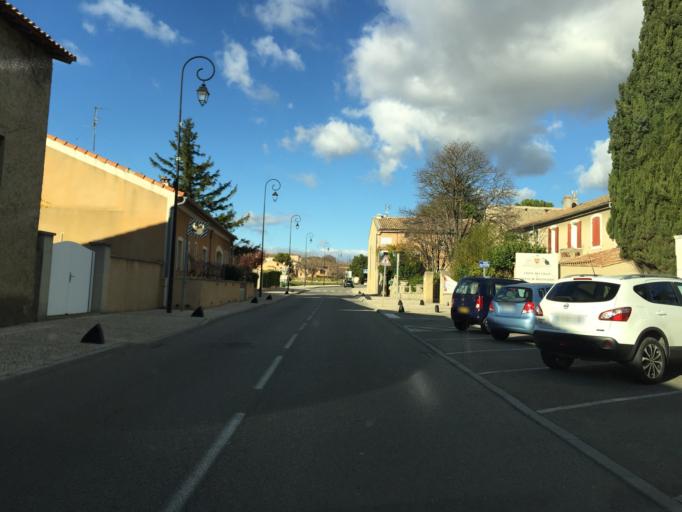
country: FR
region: Provence-Alpes-Cote d'Azur
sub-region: Departement du Vaucluse
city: Chateauneuf-du-Pape
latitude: 44.0510
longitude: 4.8354
